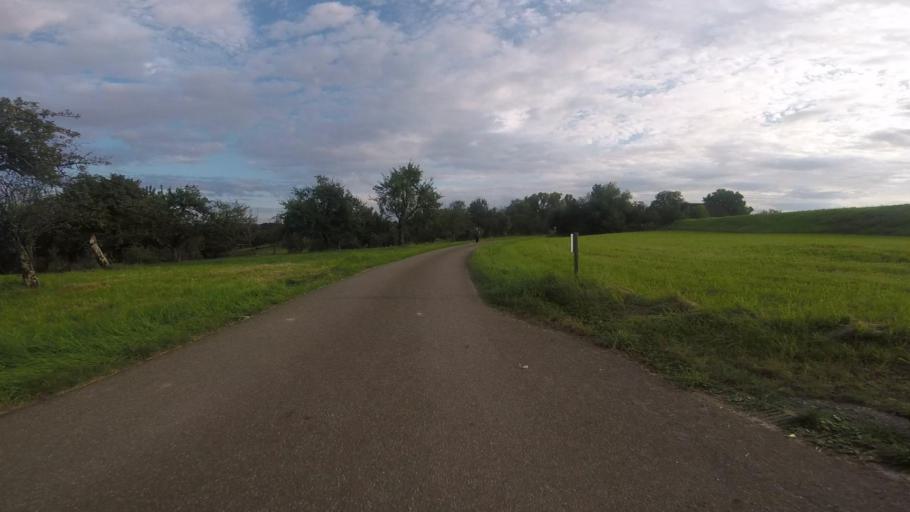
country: DE
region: Baden-Wuerttemberg
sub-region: Regierungsbezirk Stuttgart
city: Oberstenfeld
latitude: 49.0104
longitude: 9.3606
